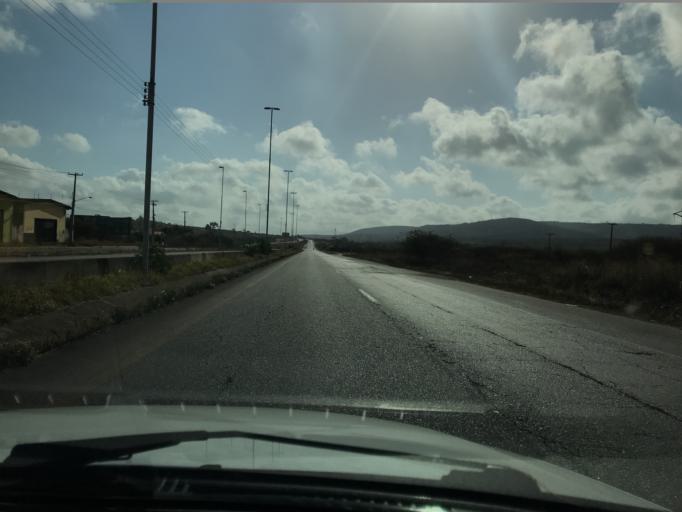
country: BR
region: Pernambuco
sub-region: Bezerros
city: Bezerros
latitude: -8.2362
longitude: -35.7293
